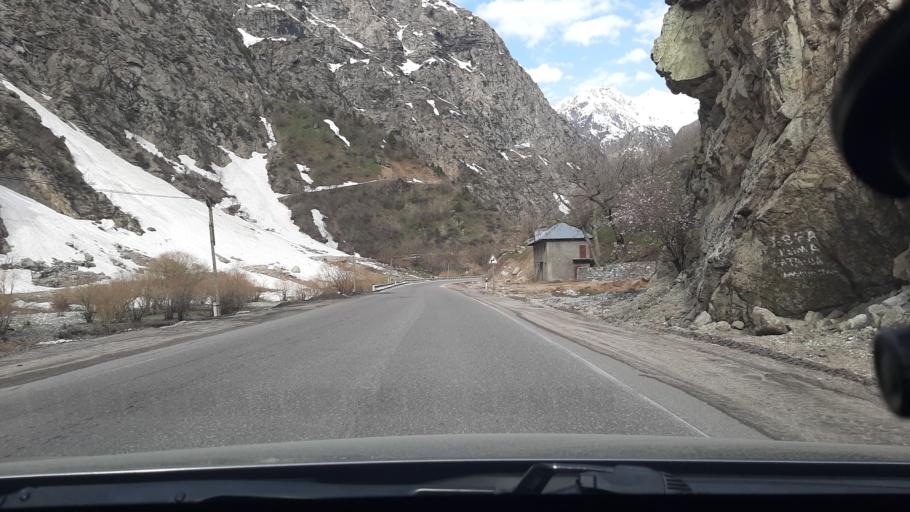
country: TJ
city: Tagob
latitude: 38.9630
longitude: 68.7736
